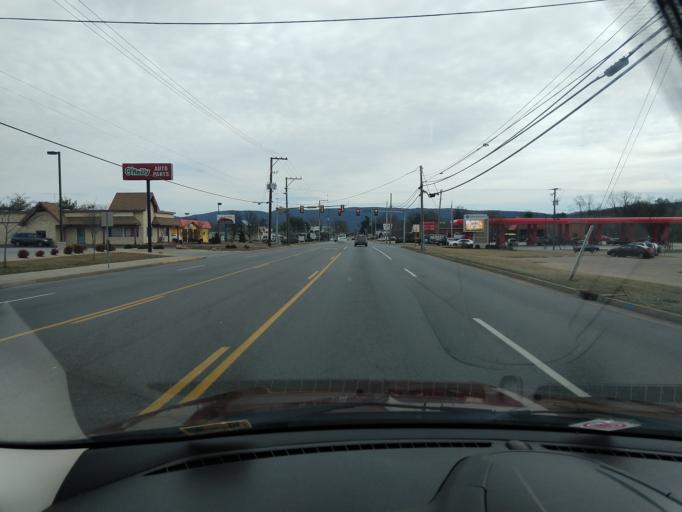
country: US
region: Virginia
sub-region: City of Waynesboro
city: Waynesboro
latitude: 38.0775
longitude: -78.9171
